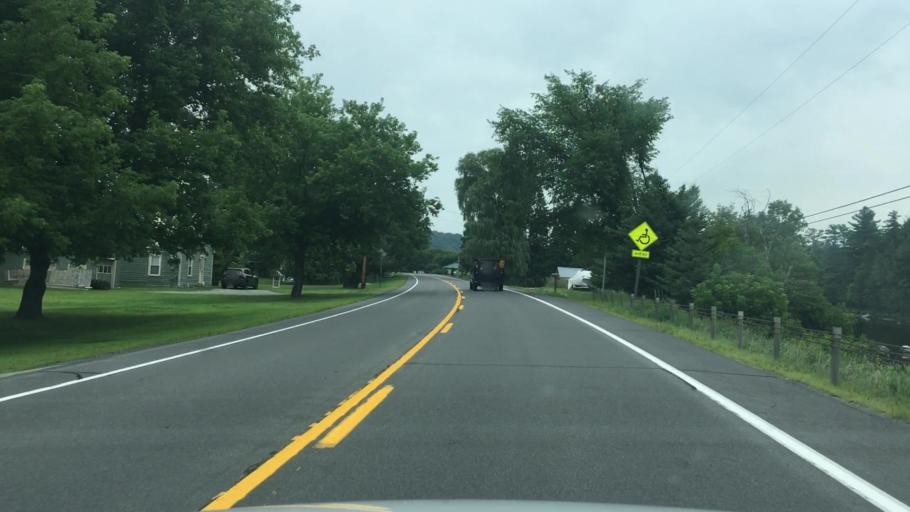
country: US
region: New York
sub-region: Essex County
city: Keeseville
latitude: 44.4561
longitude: -73.6106
